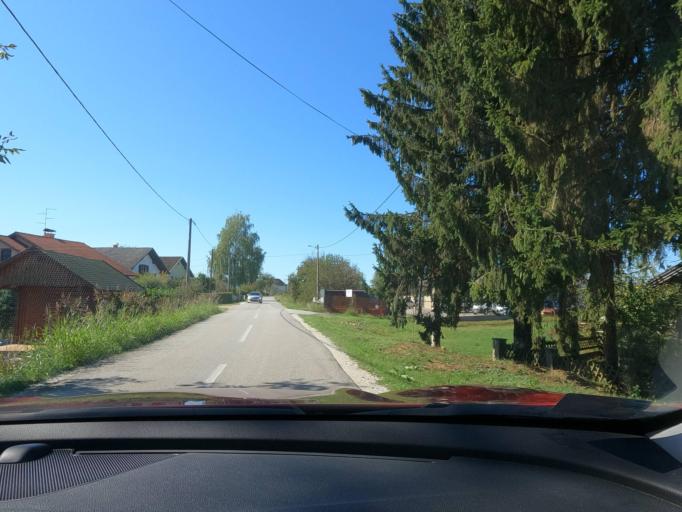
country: HR
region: Sisacko-Moslavacka
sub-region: Grad Sisak
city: Sisak
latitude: 45.4918
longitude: 16.3413
